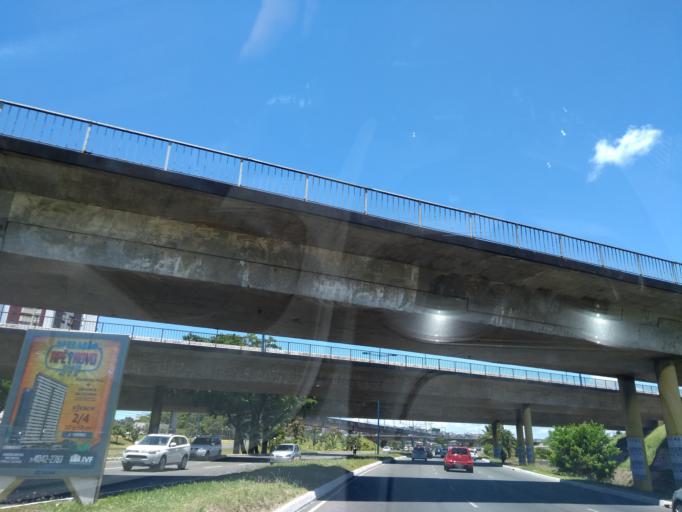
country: BR
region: Bahia
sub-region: Salvador
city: Salvador
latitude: -12.9753
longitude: -38.4767
